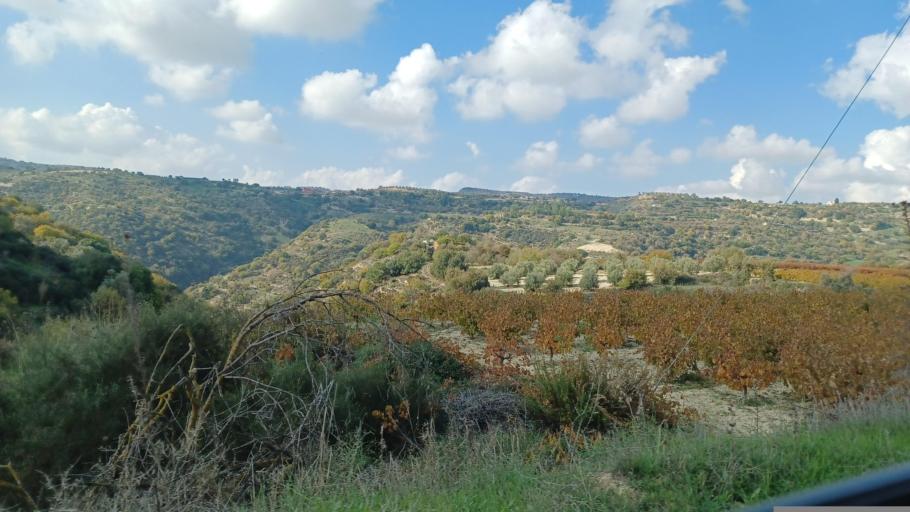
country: CY
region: Pafos
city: Mesogi
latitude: 34.8366
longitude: 32.5227
